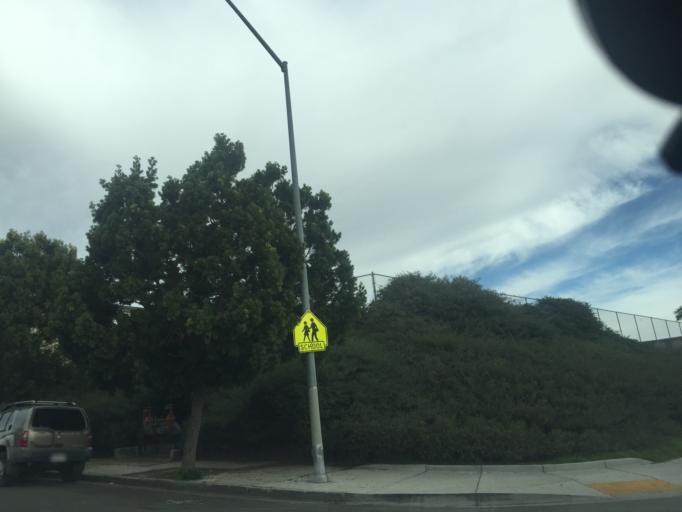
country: US
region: California
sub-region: San Diego County
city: Lemon Grove
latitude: 32.7514
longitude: -117.0902
